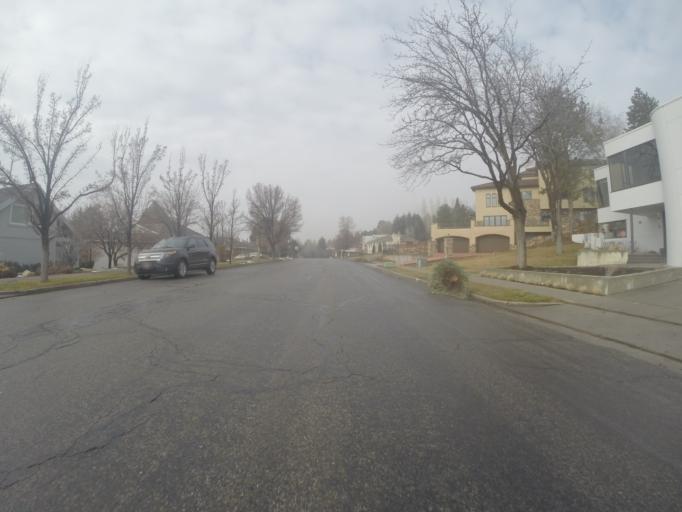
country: US
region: Utah
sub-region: Salt Lake County
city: Salt Lake City
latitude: 40.7753
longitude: -111.8435
